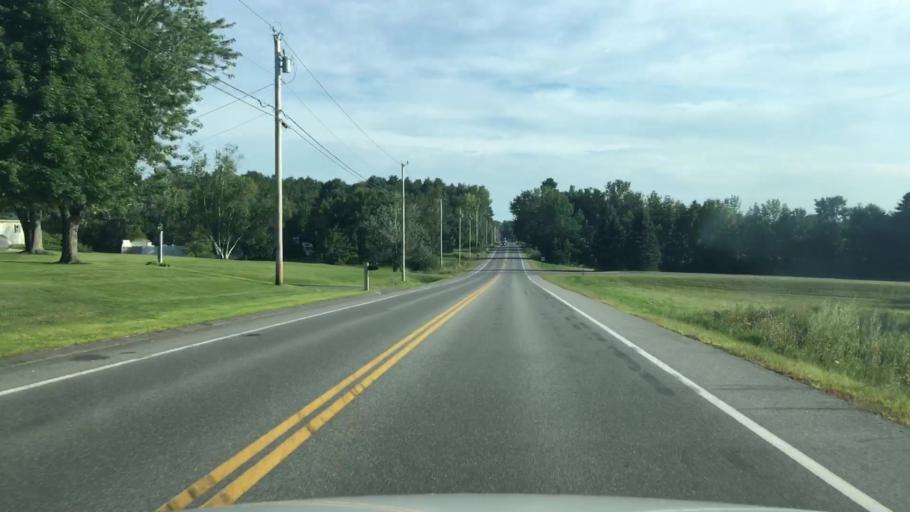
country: US
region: Maine
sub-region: Cumberland County
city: North Windham
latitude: 43.7861
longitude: -70.4397
